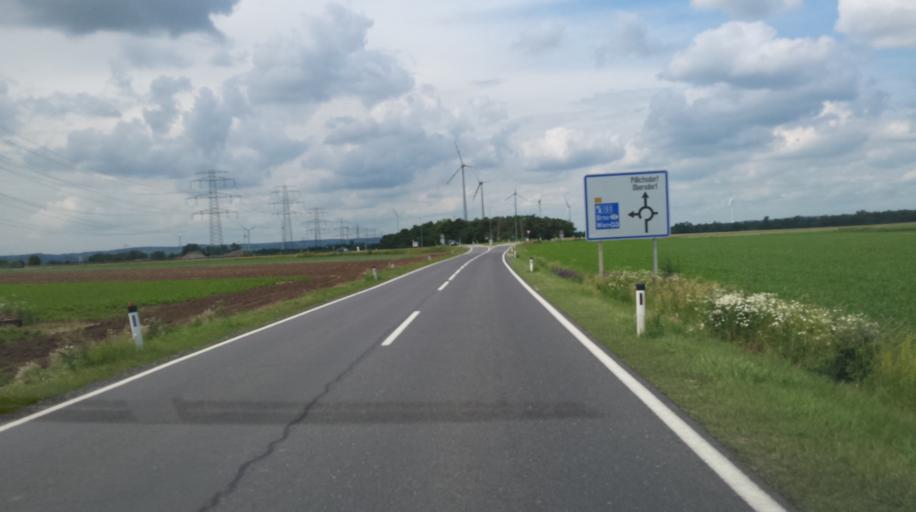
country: AT
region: Lower Austria
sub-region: Politischer Bezirk Mistelbach
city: Pillichsdorf
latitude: 48.3206
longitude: 16.5307
